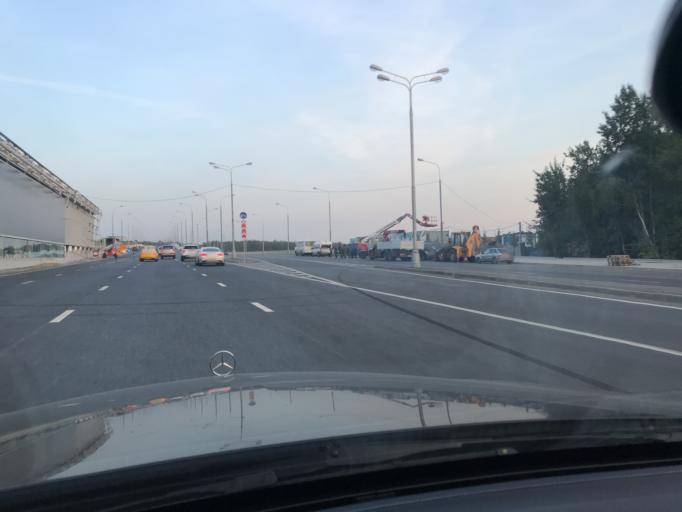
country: RU
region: Moskovskaya
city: Mosrentgen
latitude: 55.5862
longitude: 37.4333
